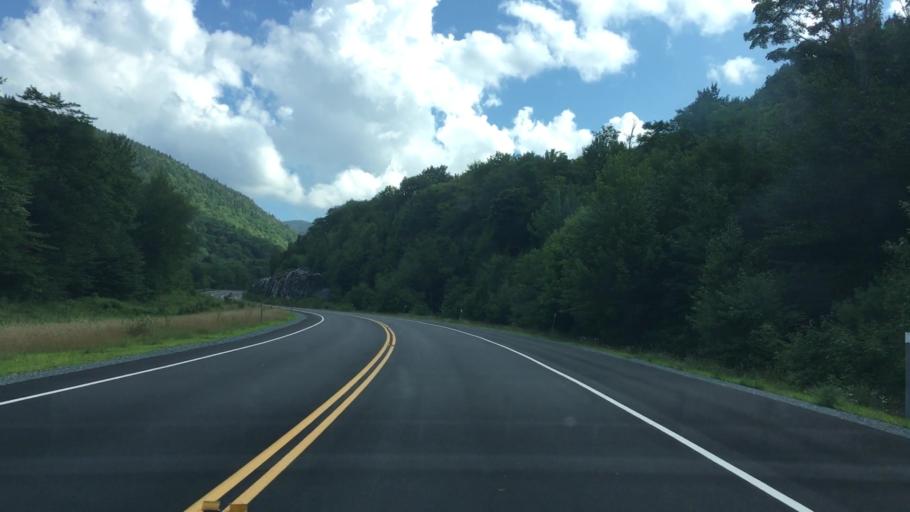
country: US
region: New Hampshire
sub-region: Grafton County
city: Woodstock
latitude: 44.0555
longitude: -71.7943
